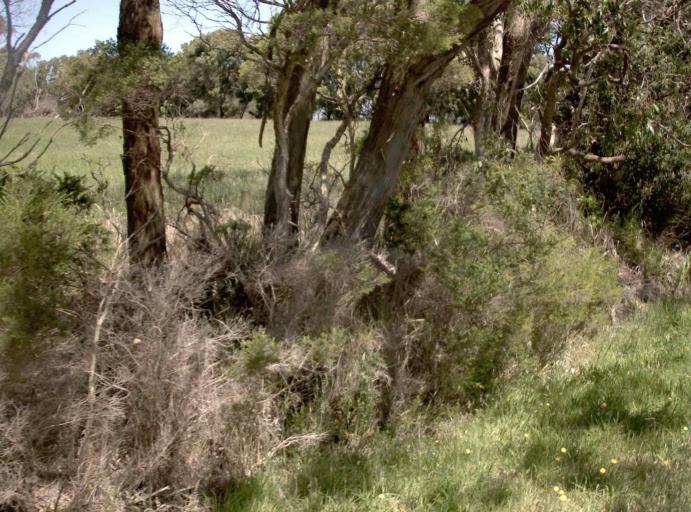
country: AU
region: Victoria
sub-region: Bass Coast
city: North Wonthaggi
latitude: -38.7540
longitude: 146.0739
